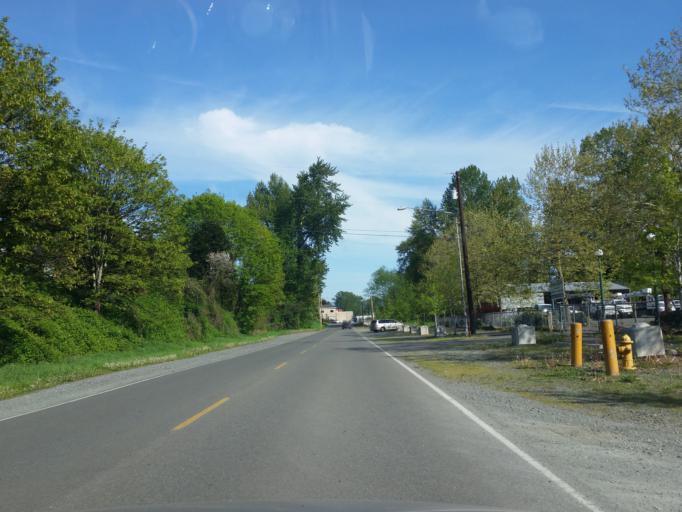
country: US
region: Washington
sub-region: Snohomish County
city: Snohomish
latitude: 47.9129
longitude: -122.1036
